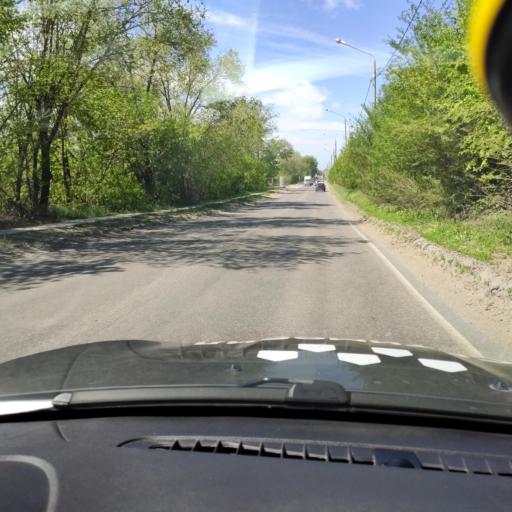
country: RU
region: Samara
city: Zhigulevsk
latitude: 53.4636
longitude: 49.5592
